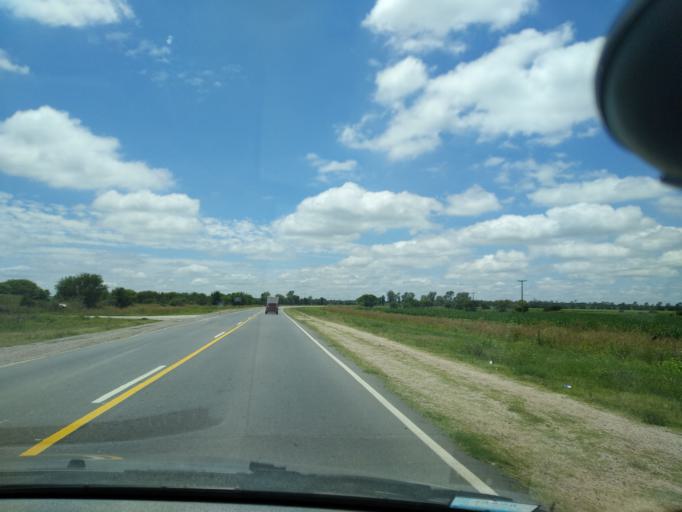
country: AR
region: Cordoba
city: Alta Gracia
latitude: -31.6543
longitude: -64.3499
